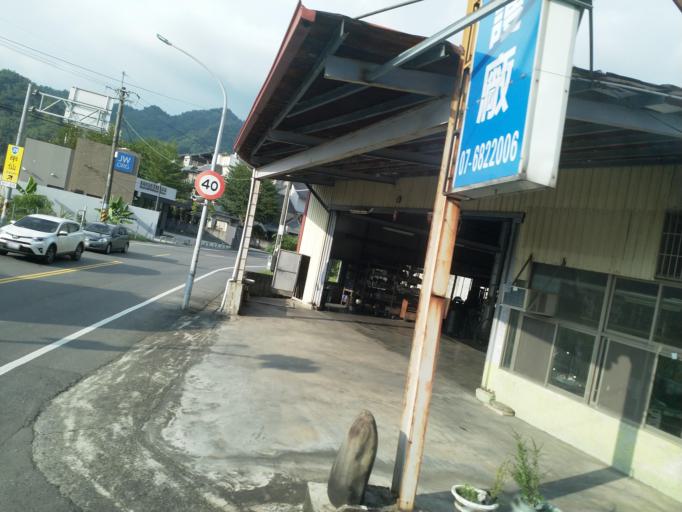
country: TW
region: Taiwan
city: Yujing
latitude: 22.9024
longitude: 120.5341
